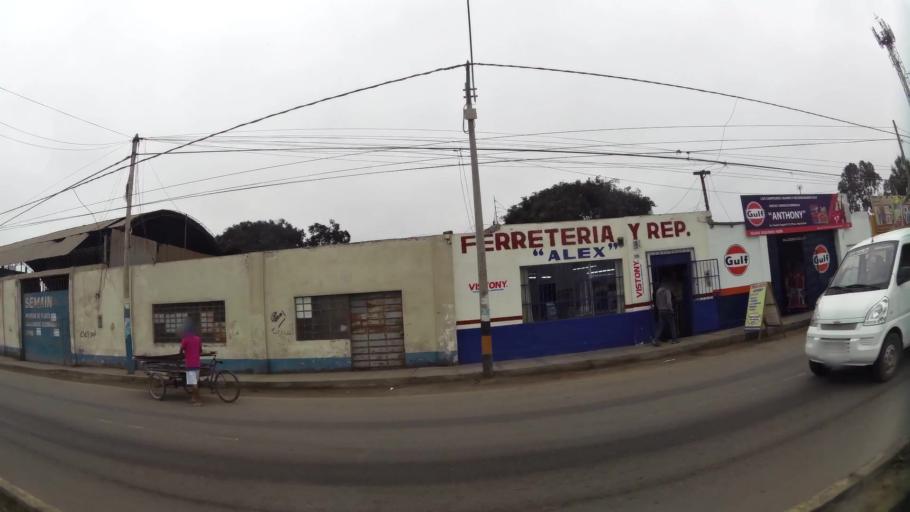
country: PE
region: Ica
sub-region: Provincia de Pisco
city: Pisco
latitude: -13.7108
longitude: -76.1974
